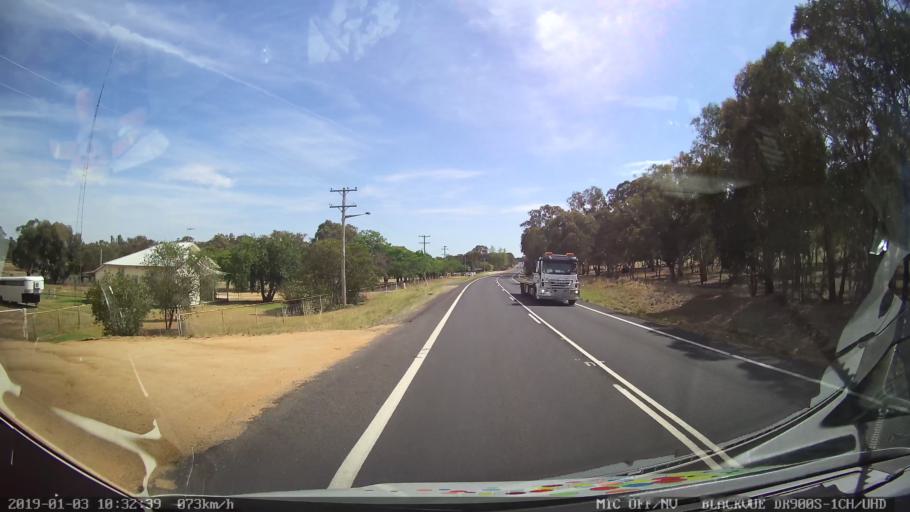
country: AU
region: New South Wales
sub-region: Young
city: Young
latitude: -34.3364
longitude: 148.2832
